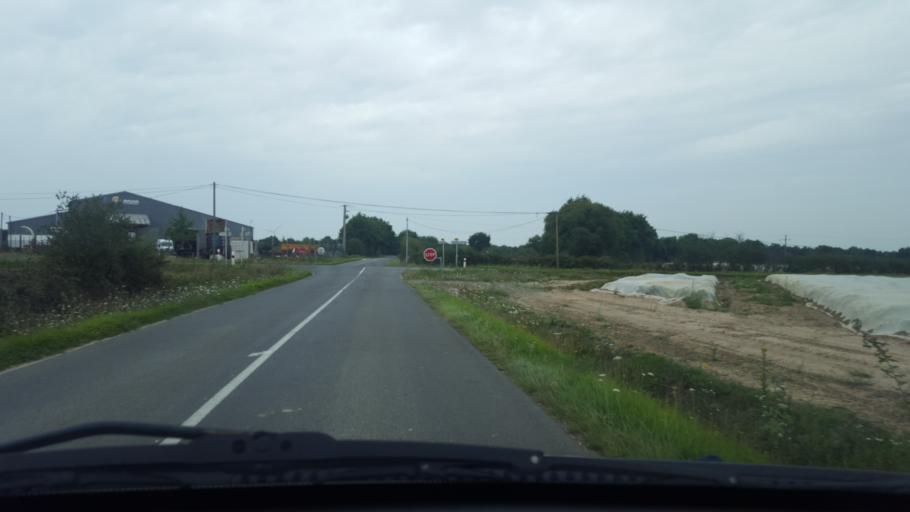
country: FR
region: Pays de la Loire
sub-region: Departement de la Loire-Atlantique
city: Saint-Philbert-de-Grand-Lieu
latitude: 46.9968
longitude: -1.6621
